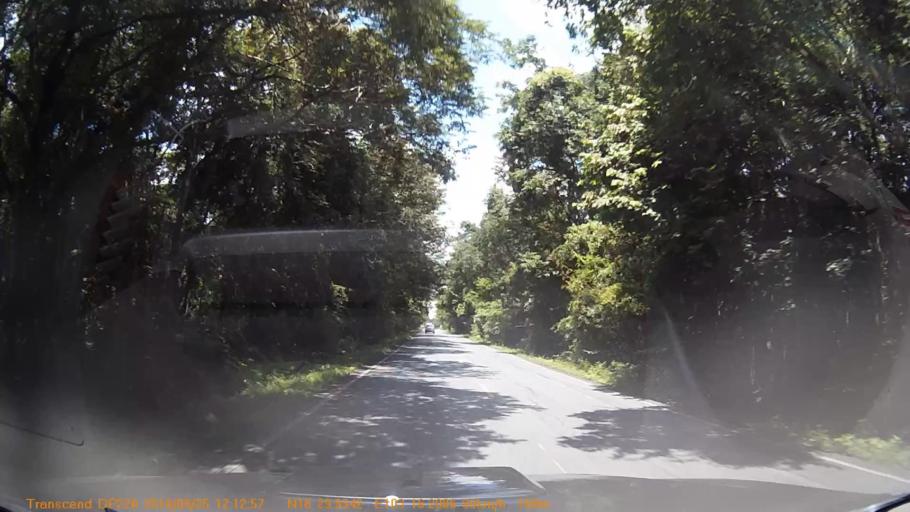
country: TH
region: Kalasin
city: Huai Mek
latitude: 16.4989
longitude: 103.2701
